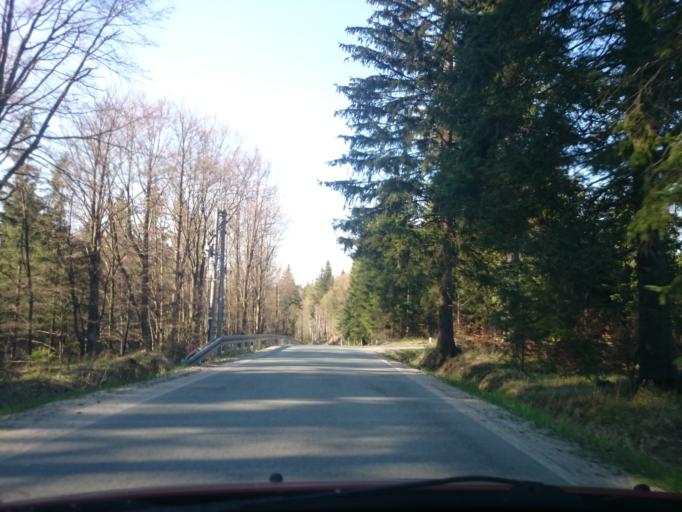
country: PL
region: Lower Silesian Voivodeship
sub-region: Powiat klodzki
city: Duszniki-Zdroj
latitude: 50.3328
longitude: 16.4054
